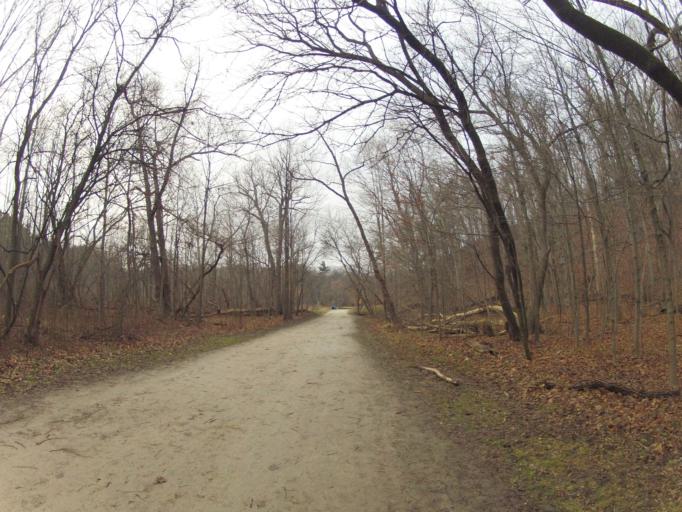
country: CA
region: Ontario
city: Mississauga
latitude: 43.5565
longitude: -79.6666
